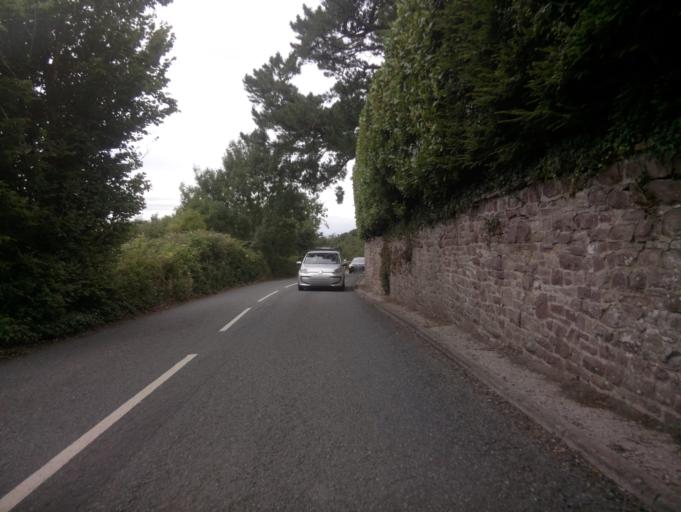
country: GB
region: England
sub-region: North Somerset
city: Churchill
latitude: 51.3099
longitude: -2.7998
